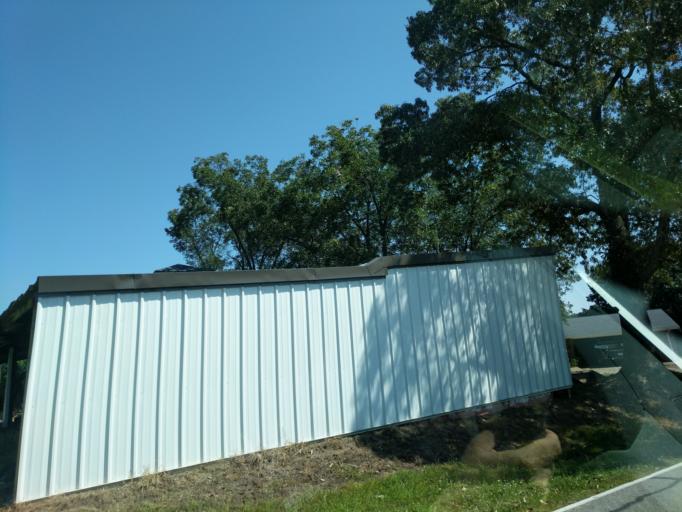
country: US
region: South Carolina
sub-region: Spartanburg County
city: Valley Falls
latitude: 35.0130
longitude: -81.9297
